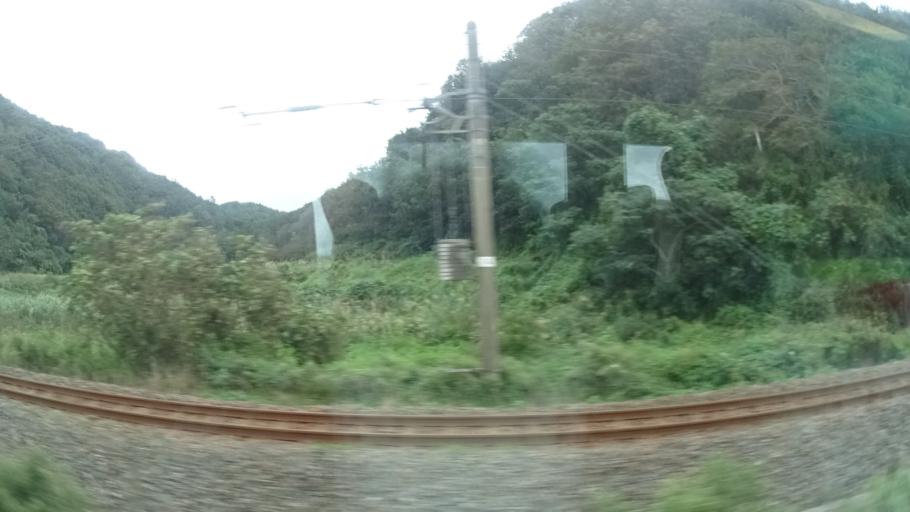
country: JP
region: Yamagata
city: Tsuruoka
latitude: 38.5784
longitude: 139.5596
